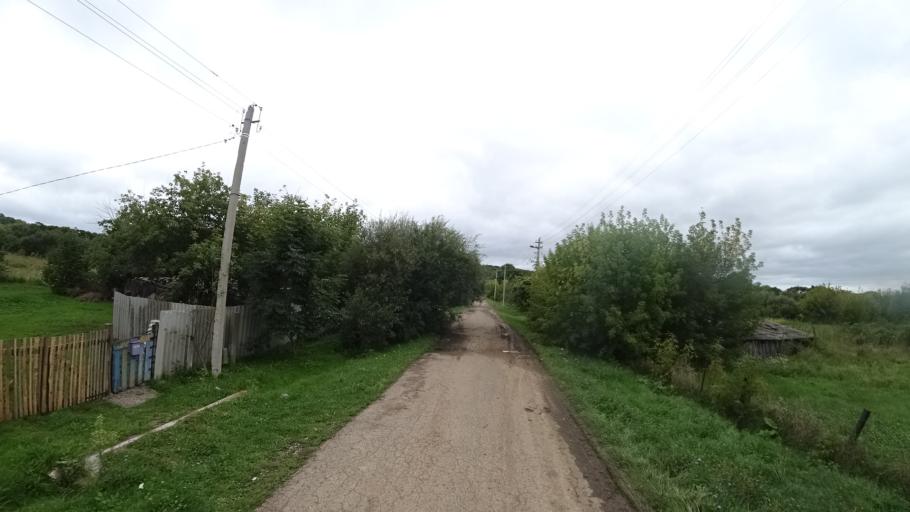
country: RU
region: Primorskiy
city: Chernigovka
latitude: 44.4552
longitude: 132.5914
